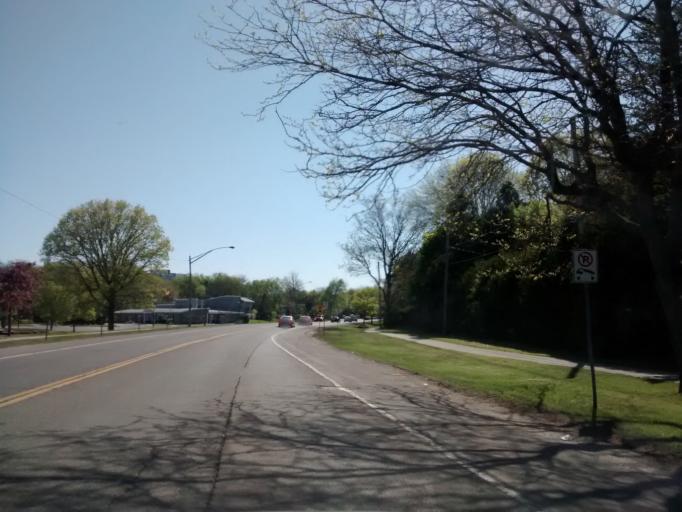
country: CA
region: Ontario
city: Oakville
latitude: 43.4063
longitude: -79.6955
